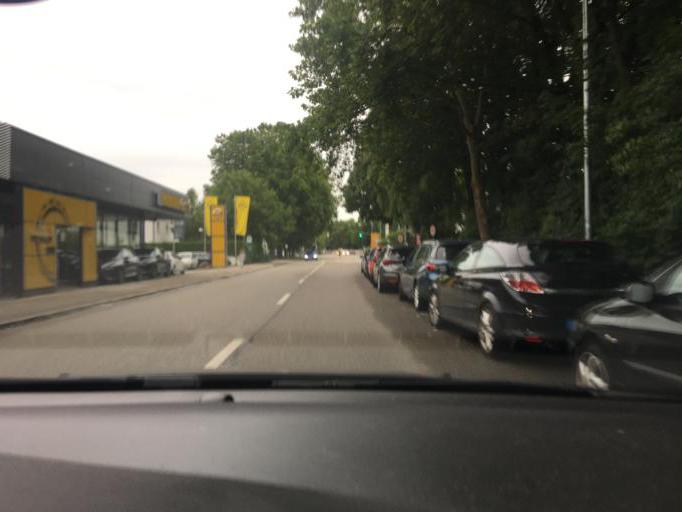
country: DE
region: Bavaria
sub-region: Upper Bavaria
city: Erding
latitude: 48.3092
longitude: 11.9158
